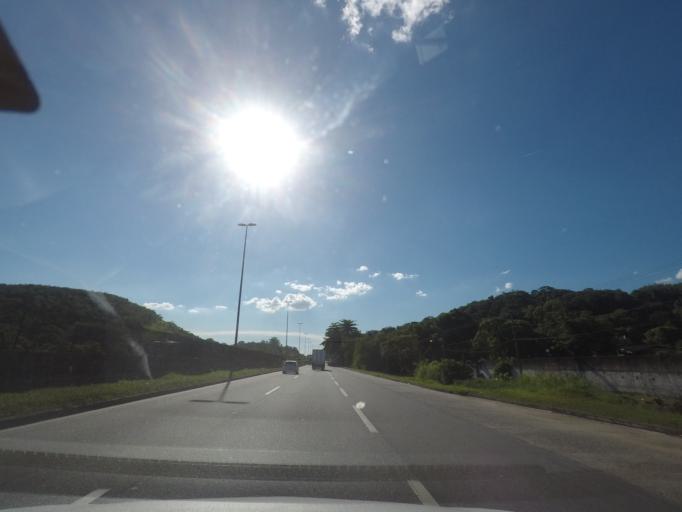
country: BR
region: Rio de Janeiro
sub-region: Petropolis
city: Petropolis
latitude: -22.6536
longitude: -43.1530
